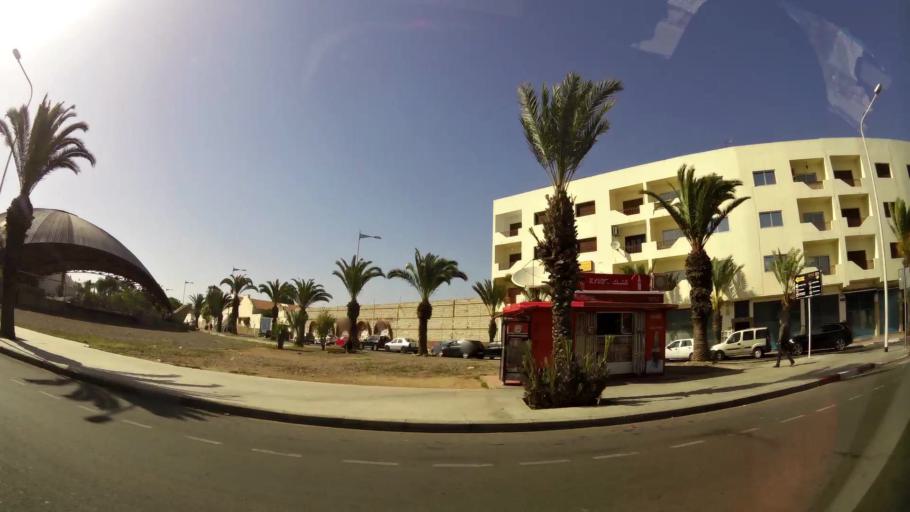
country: MA
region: Souss-Massa-Draa
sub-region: Agadir-Ida-ou-Tnan
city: Agadir
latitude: 30.4149
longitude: -9.5836
